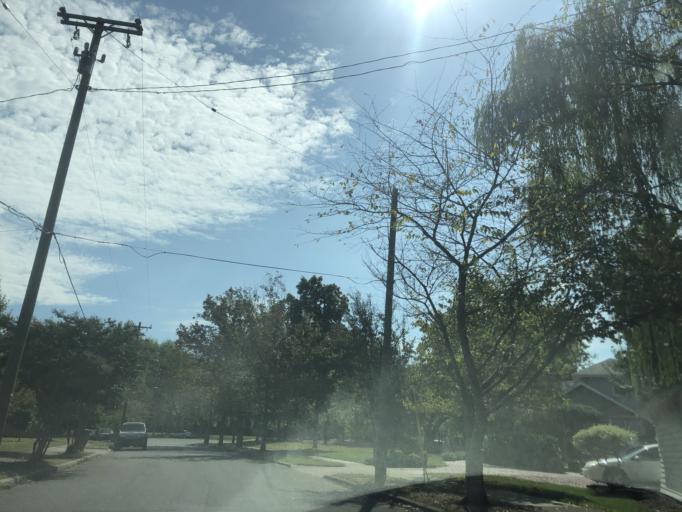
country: US
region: Tennessee
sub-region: Davidson County
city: Belle Meade
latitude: 36.1371
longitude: -86.8323
